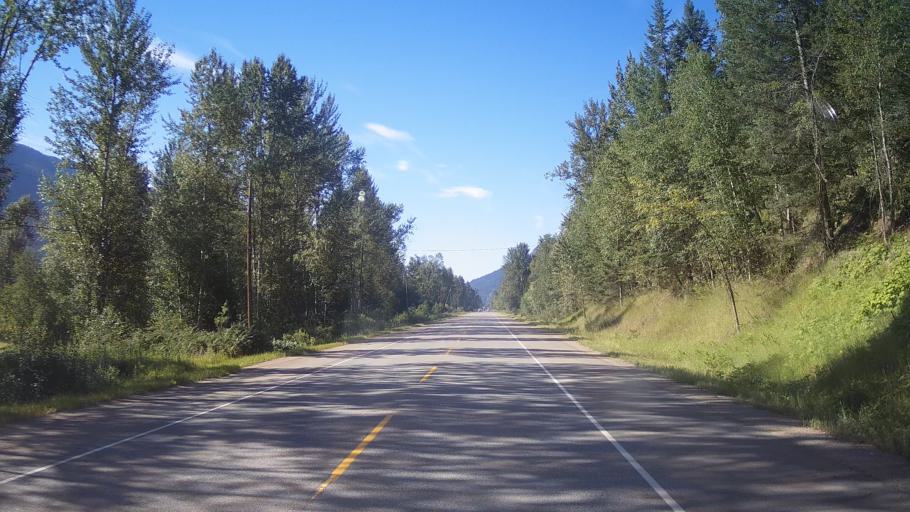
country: CA
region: British Columbia
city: Chase
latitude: 51.5261
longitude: -120.1710
